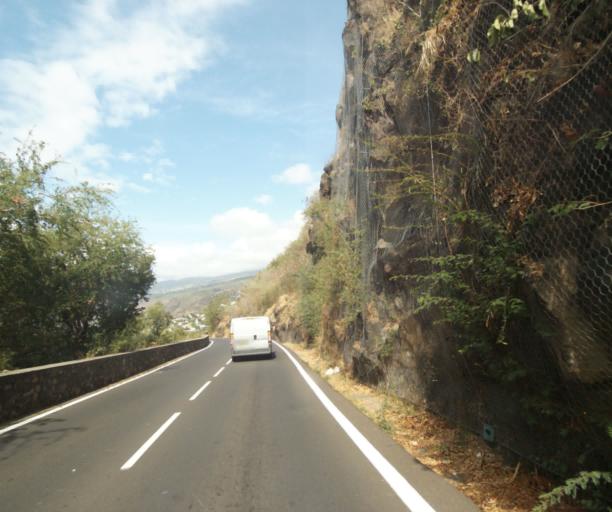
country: RE
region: Reunion
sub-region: Reunion
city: Saint-Paul
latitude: -21.0161
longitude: 55.2697
